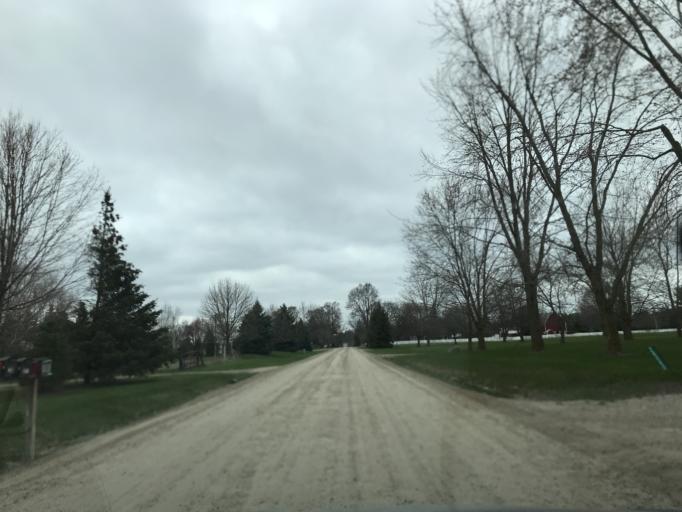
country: US
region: Michigan
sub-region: Oakland County
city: South Lyon
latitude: 42.4906
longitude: -83.6688
